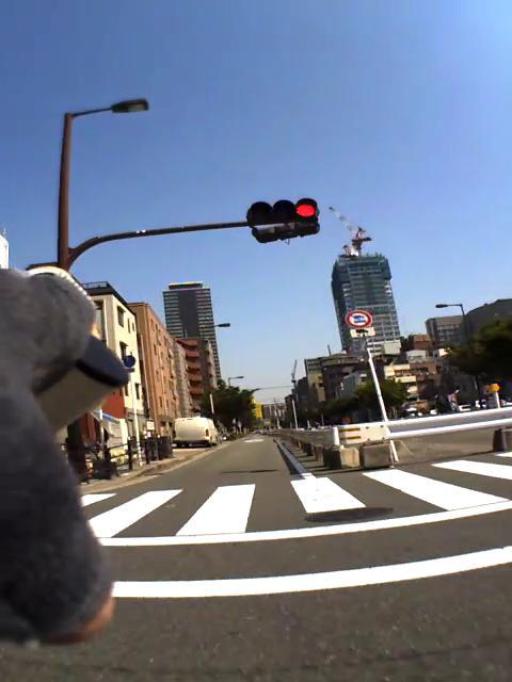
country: JP
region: Osaka
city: Osaka-shi
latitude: 34.7024
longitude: 135.5058
